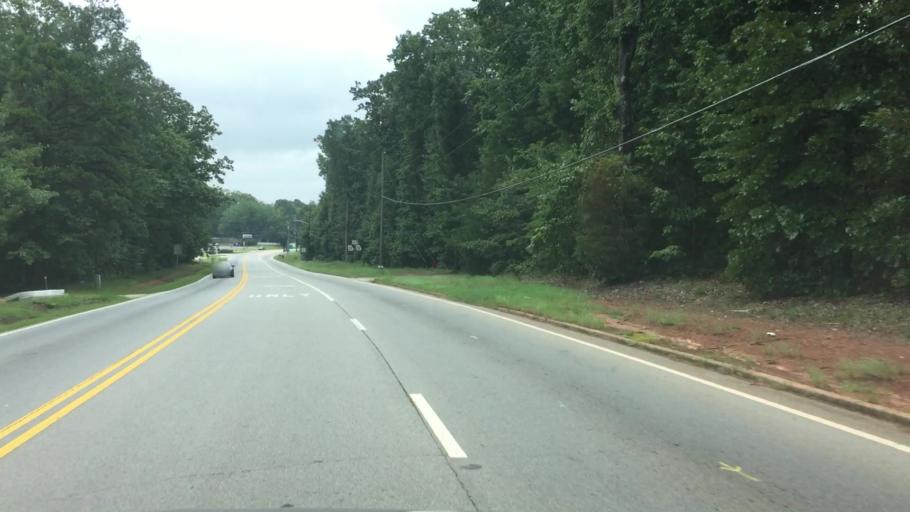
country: US
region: Georgia
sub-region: Barrow County
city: Winder
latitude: 34.0118
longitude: -83.7073
